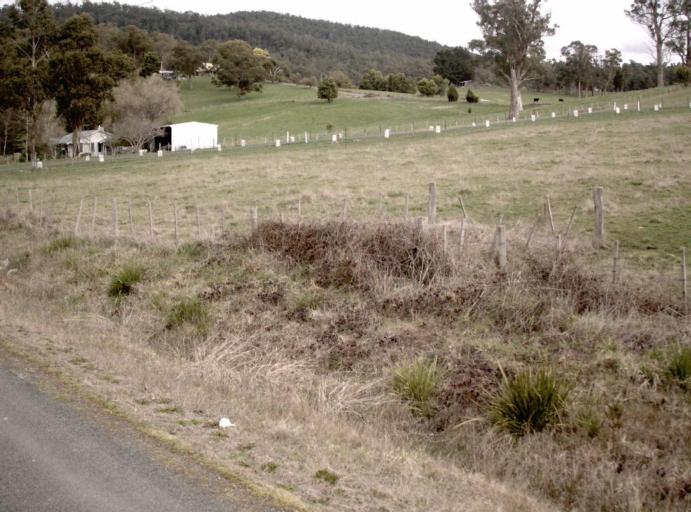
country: AU
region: Tasmania
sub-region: Launceston
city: Mayfield
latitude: -41.2638
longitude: 147.1606
